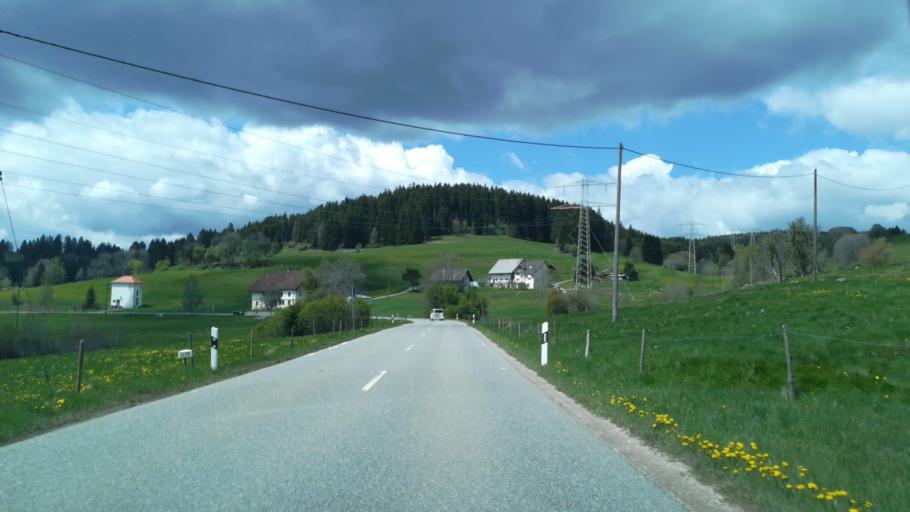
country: DE
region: Baden-Wuerttemberg
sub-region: Freiburg Region
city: Grafenhausen
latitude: 47.7965
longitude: 8.2334
